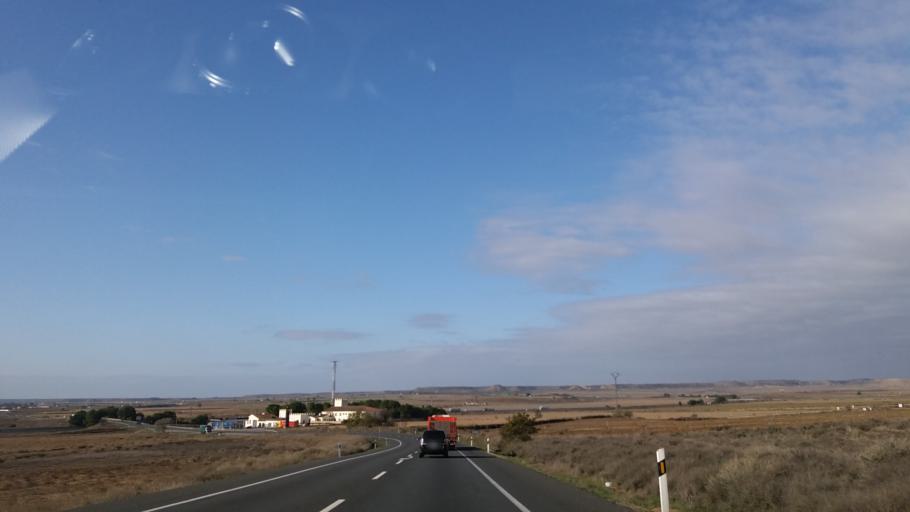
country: ES
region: Aragon
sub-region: Provincia de Huesca
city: Candasnos
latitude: 41.5134
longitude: 0.0940
